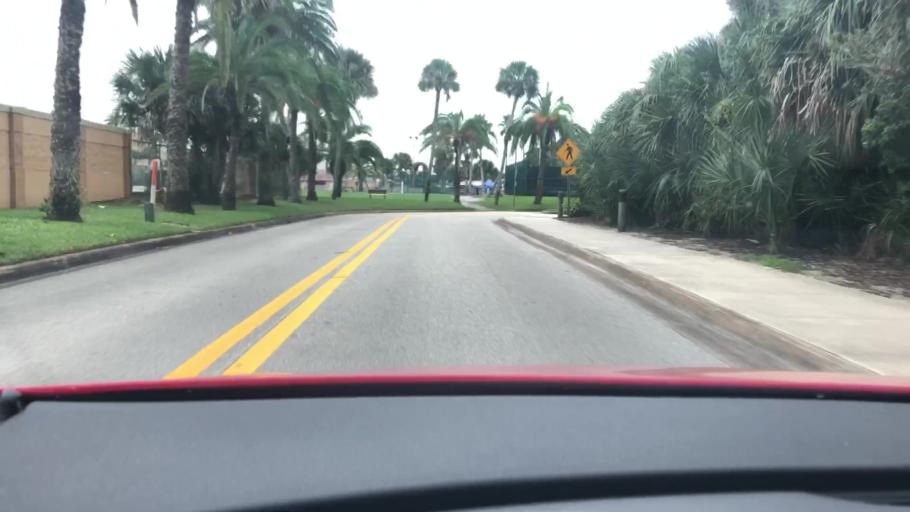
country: US
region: Florida
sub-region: Volusia County
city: Daytona Beach Shores
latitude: 29.1665
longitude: -80.9795
